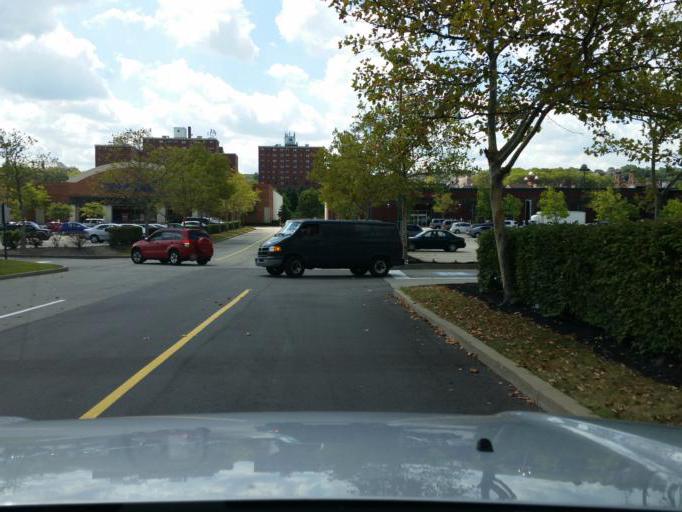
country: US
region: Pennsylvania
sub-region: Allegheny County
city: Homestead
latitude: 40.4126
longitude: -79.9084
